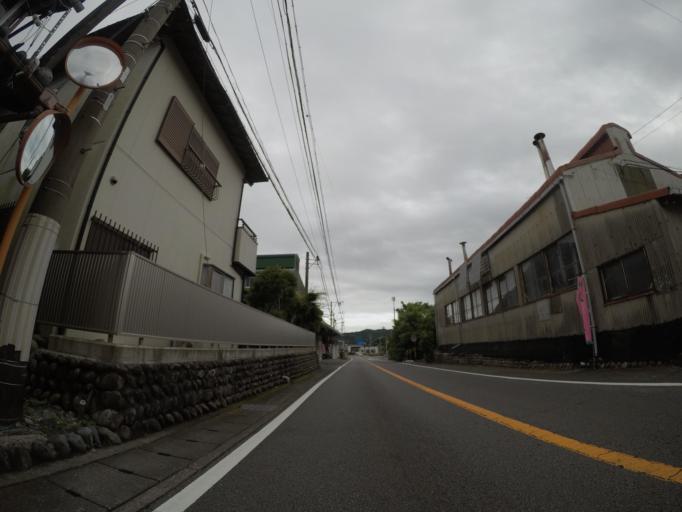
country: JP
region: Shizuoka
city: Sagara
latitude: 34.7309
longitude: 138.1618
